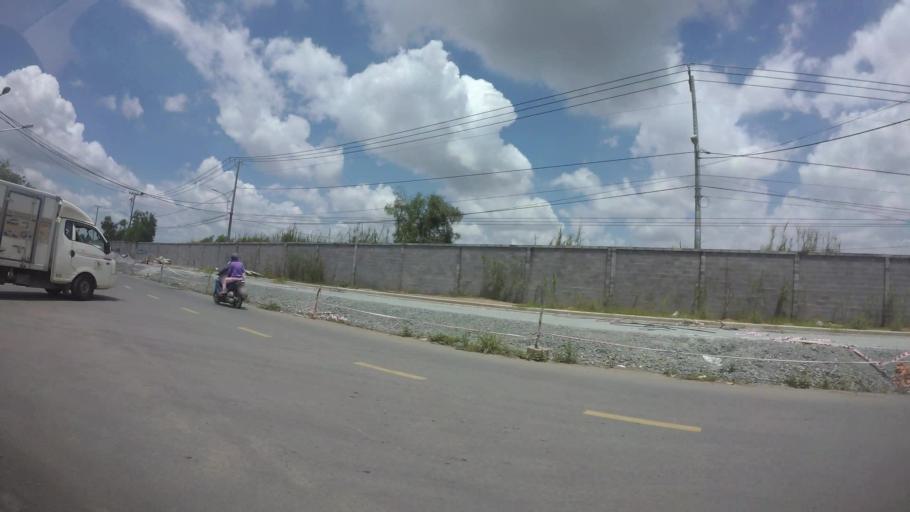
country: VN
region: Ho Chi Minh City
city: Quan Hai
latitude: 10.8056
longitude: 106.7778
